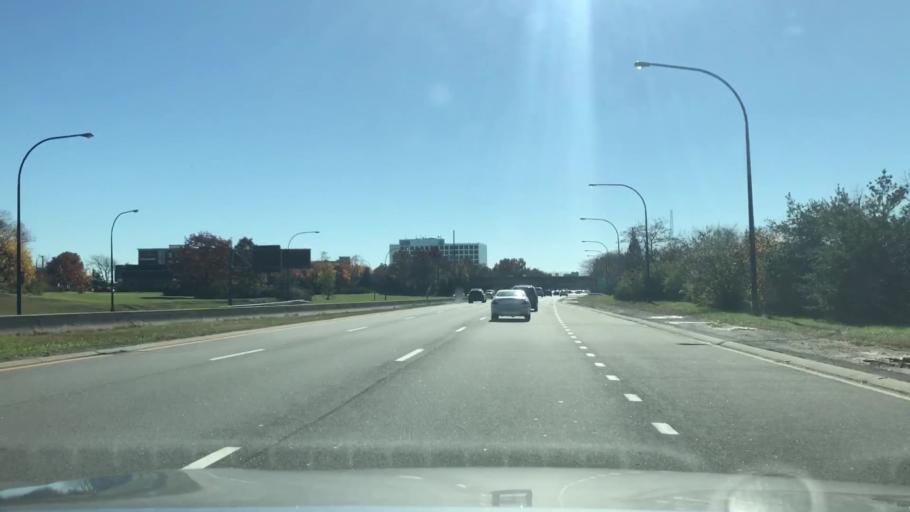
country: US
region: New York
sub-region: Nassau County
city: East Garden City
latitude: 40.7247
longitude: -73.5806
